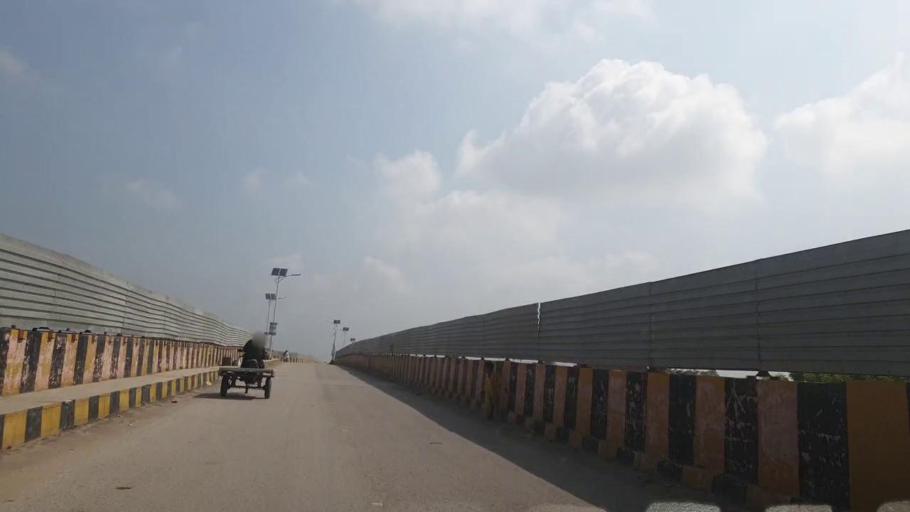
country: PK
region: Sindh
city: Khairpur
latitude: 27.5262
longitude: 68.7433
